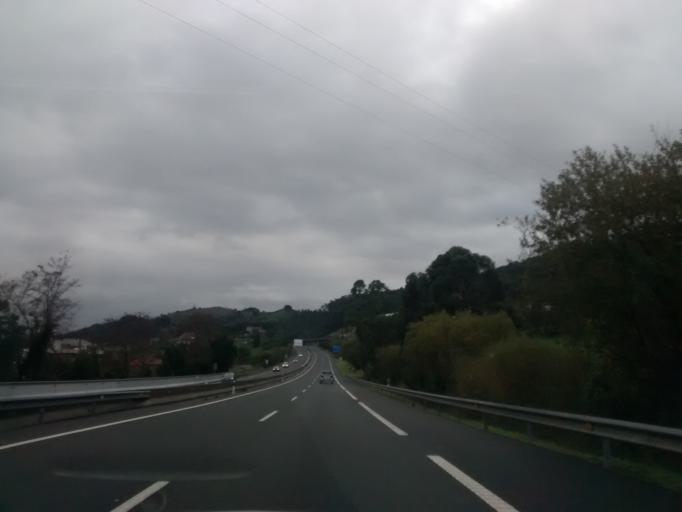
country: ES
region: Cantabria
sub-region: Provincia de Cantabria
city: Castro-Urdiales
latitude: 43.3895
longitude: -3.2342
